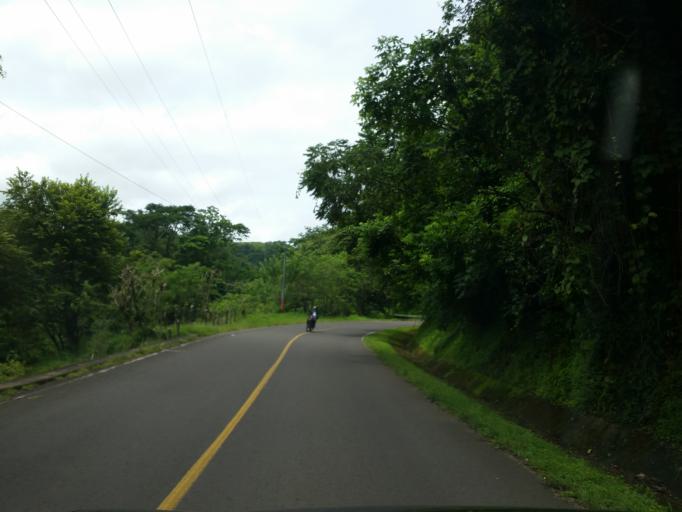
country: NI
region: Matagalpa
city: San Ramon
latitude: 13.0236
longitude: -85.7852
